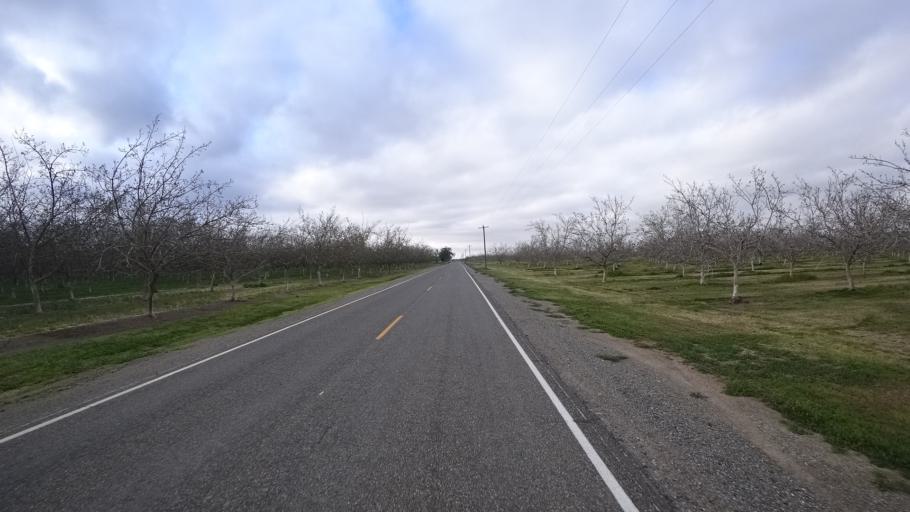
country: US
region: California
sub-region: Glenn County
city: Willows
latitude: 39.4615
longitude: -121.9678
